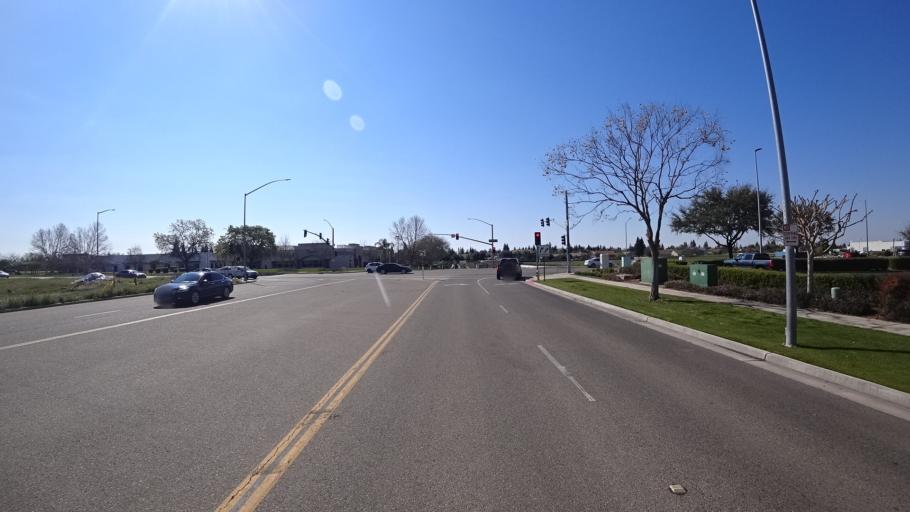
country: US
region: California
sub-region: Fresno County
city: Clovis
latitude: 36.8380
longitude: -119.7248
